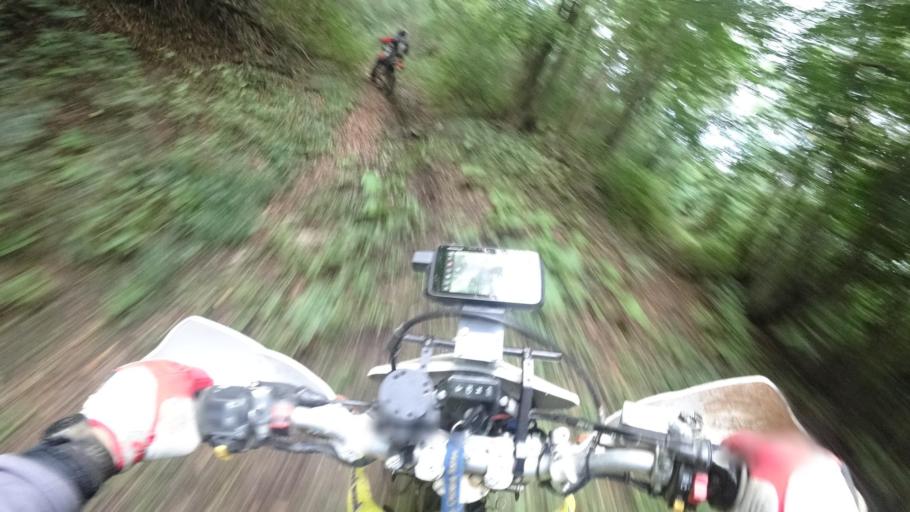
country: BA
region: Republika Srpska
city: Starcevica
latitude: 44.7114
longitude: 17.2232
